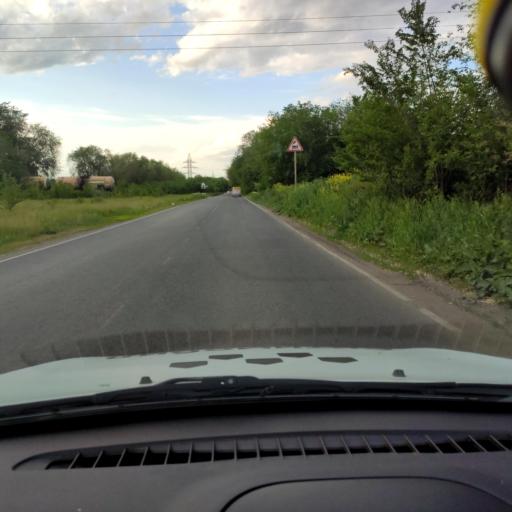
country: RU
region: Samara
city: Tol'yatti
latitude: 53.5780
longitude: 49.2554
